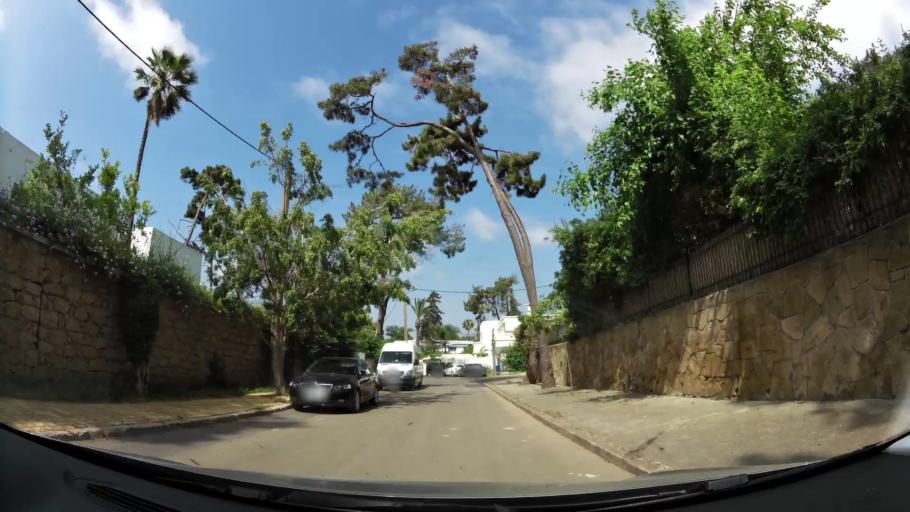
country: MA
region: Rabat-Sale-Zemmour-Zaer
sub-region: Rabat
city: Rabat
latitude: 33.9838
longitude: -6.8318
